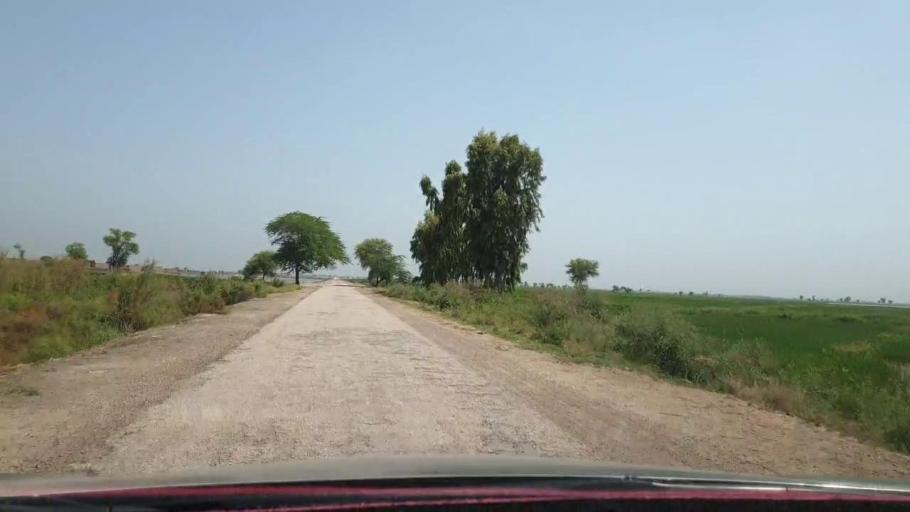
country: PK
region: Sindh
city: Warah
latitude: 27.3808
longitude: 67.7865
